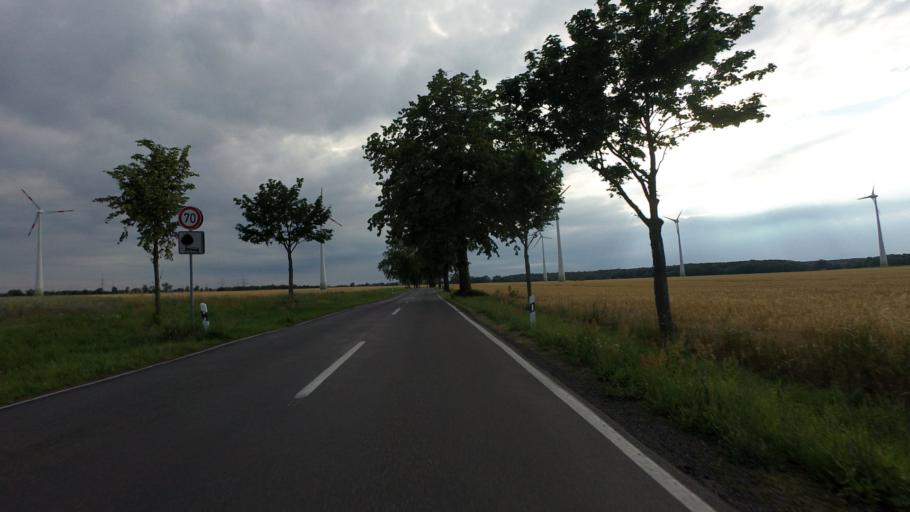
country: DE
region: Brandenburg
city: Nauen
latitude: 52.5900
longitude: 12.8011
